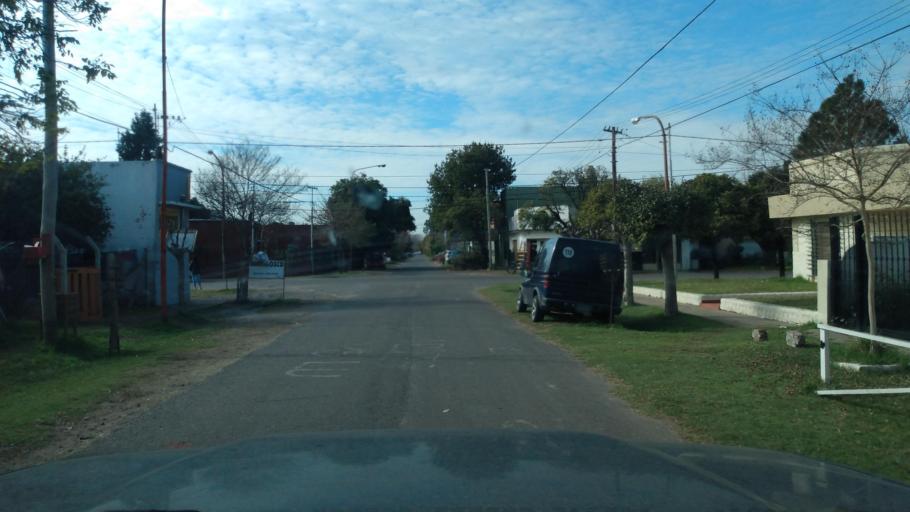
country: AR
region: Buenos Aires
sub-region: Partido de Lujan
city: Lujan
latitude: -34.5975
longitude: -59.1810
